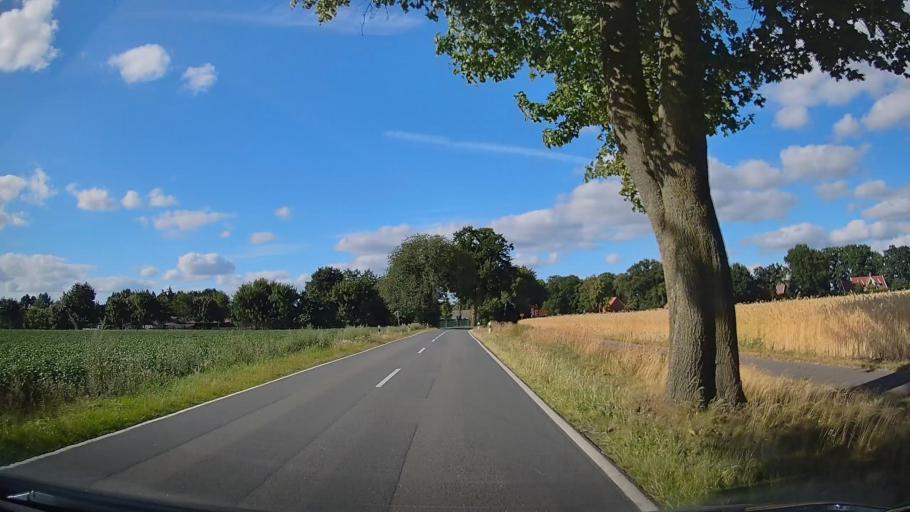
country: DE
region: Lower Saxony
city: Vrees
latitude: 52.8188
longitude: 7.7818
